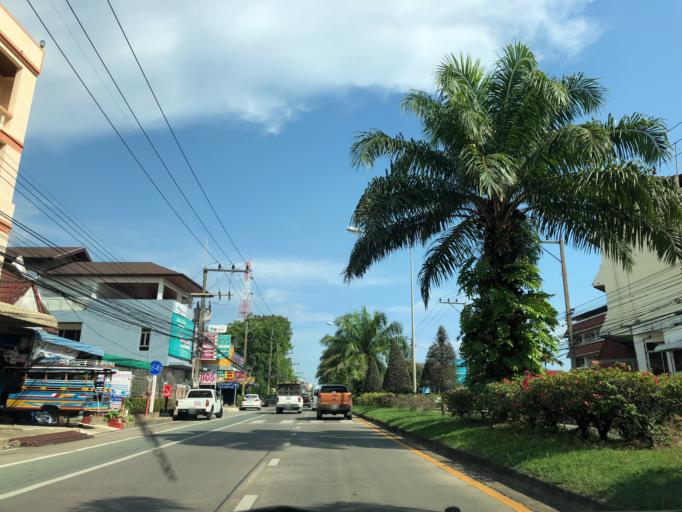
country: TH
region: Krabi
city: Krabi
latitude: 8.0845
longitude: 98.9138
